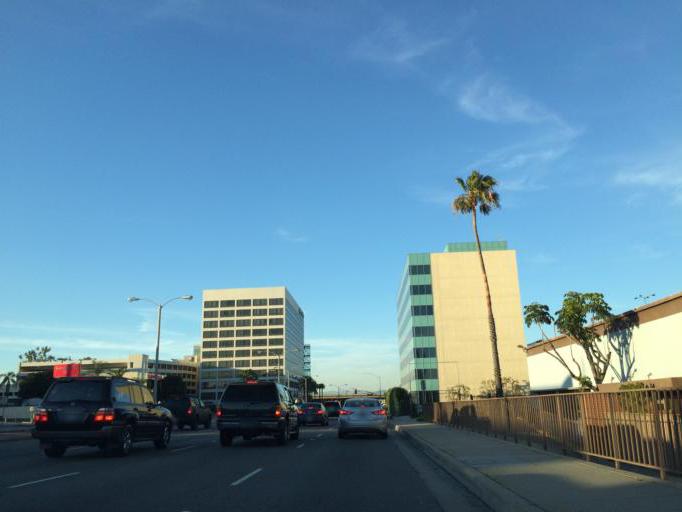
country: US
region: California
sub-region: Los Angeles County
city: El Segundo
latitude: 33.9274
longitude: -118.3961
